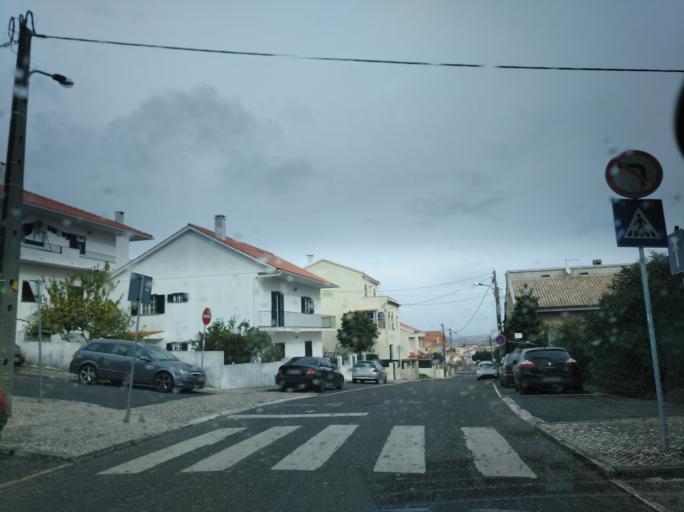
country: PT
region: Lisbon
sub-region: Odivelas
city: Famoes
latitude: 38.7959
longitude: -9.2181
